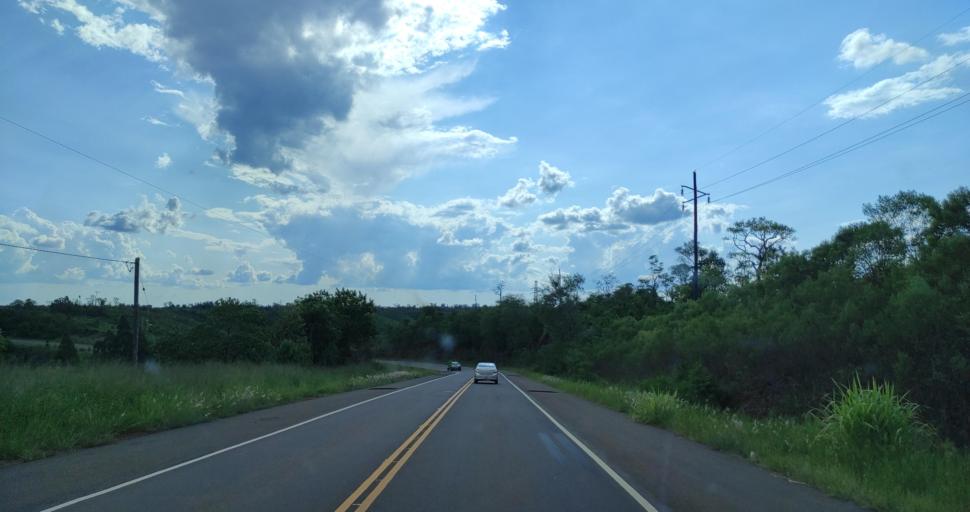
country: AR
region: Misiones
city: Bernardo de Irigoyen
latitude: -26.2986
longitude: -53.8121
